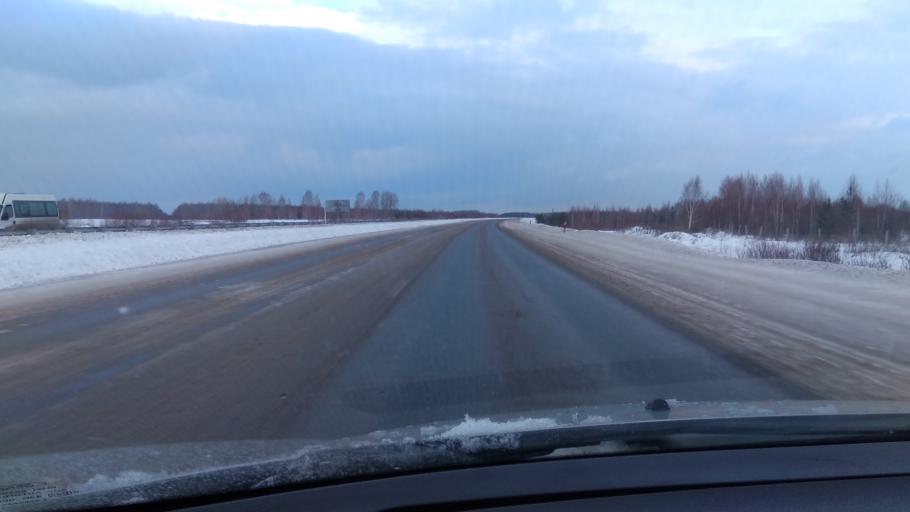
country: RU
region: Sverdlovsk
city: Nev'yansk
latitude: 57.5149
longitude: 60.1782
